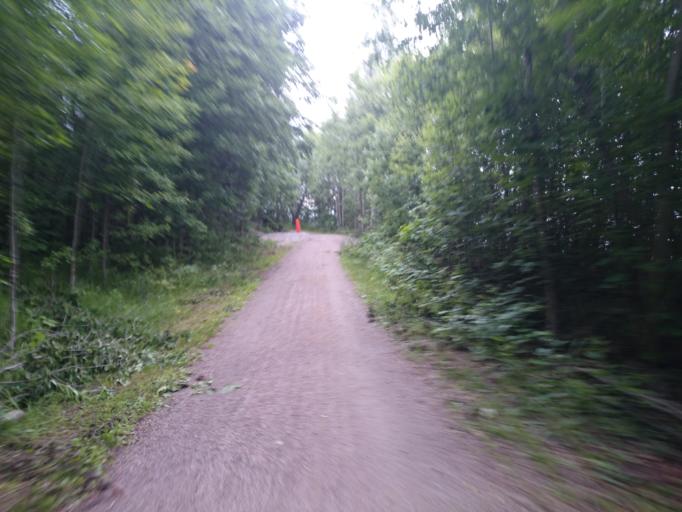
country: SE
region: Vaesternorrland
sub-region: Sundsvalls Kommun
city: Stockvik
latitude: 62.3230
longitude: 17.3707
